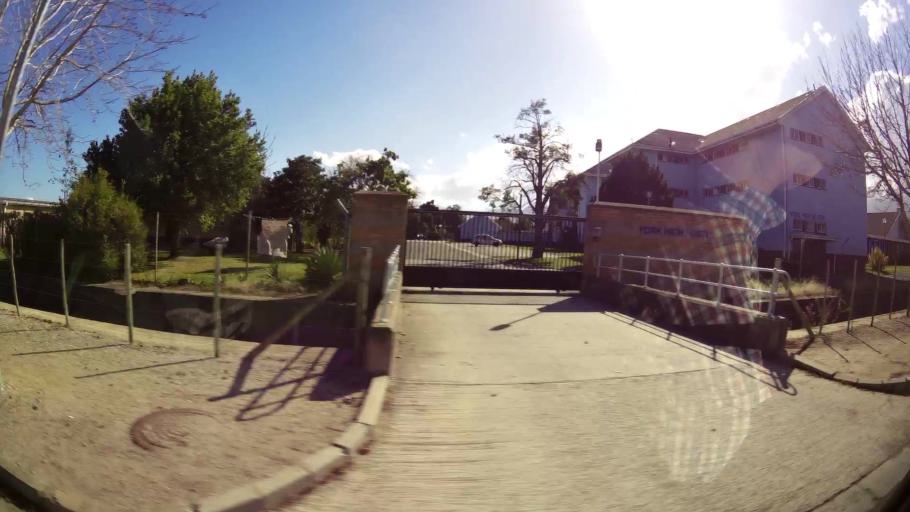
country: ZA
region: Western Cape
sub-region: Eden District Municipality
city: George
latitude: -33.9741
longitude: 22.4491
